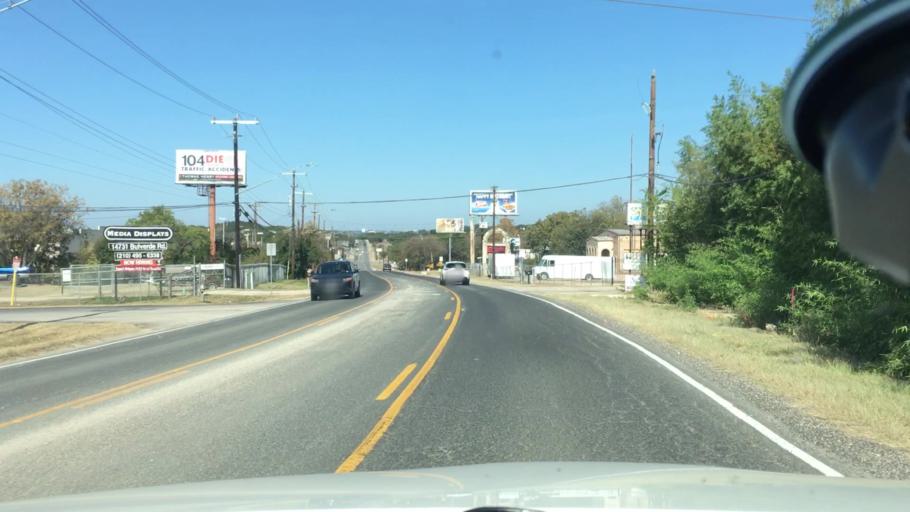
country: US
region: Texas
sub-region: Bexar County
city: Windcrest
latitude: 29.5742
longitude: -98.4182
